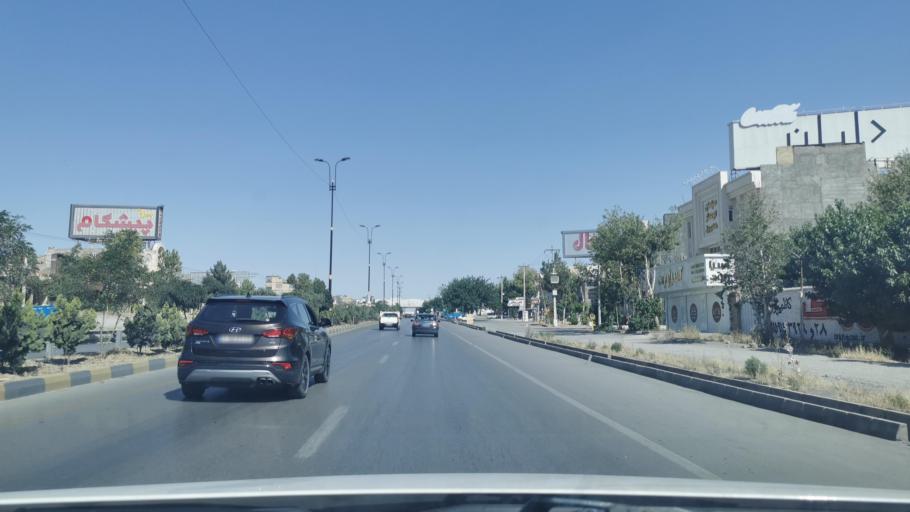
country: IR
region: Razavi Khorasan
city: Torqabeh
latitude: 36.3960
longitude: 59.3968
